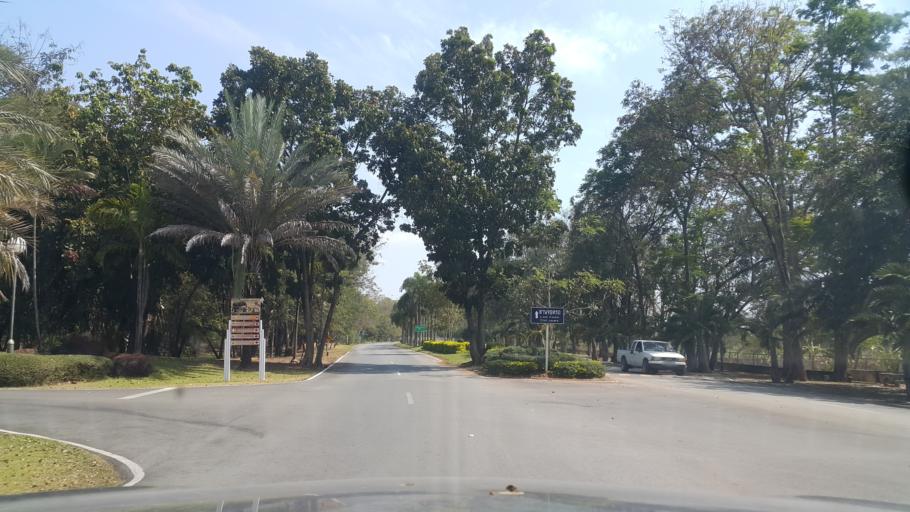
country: TH
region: Nakhon Ratchasima
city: Nakhon Ratchasima
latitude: 14.8502
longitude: 102.0783
